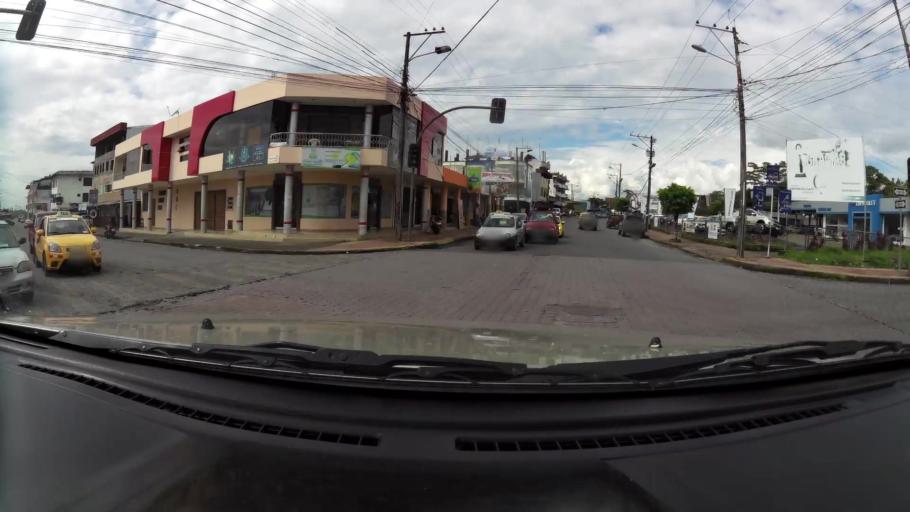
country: EC
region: Pastaza
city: Puyo
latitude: -1.4879
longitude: -78.0079
